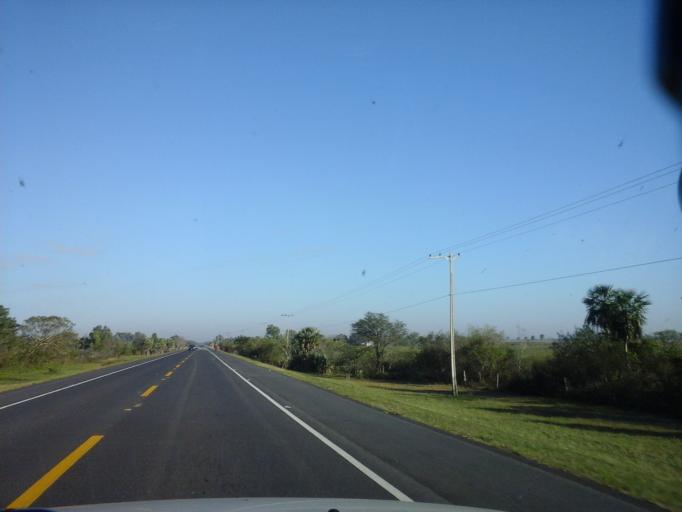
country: PY
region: Neembucu
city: Pilar
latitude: -26.8553
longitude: -58.0313
